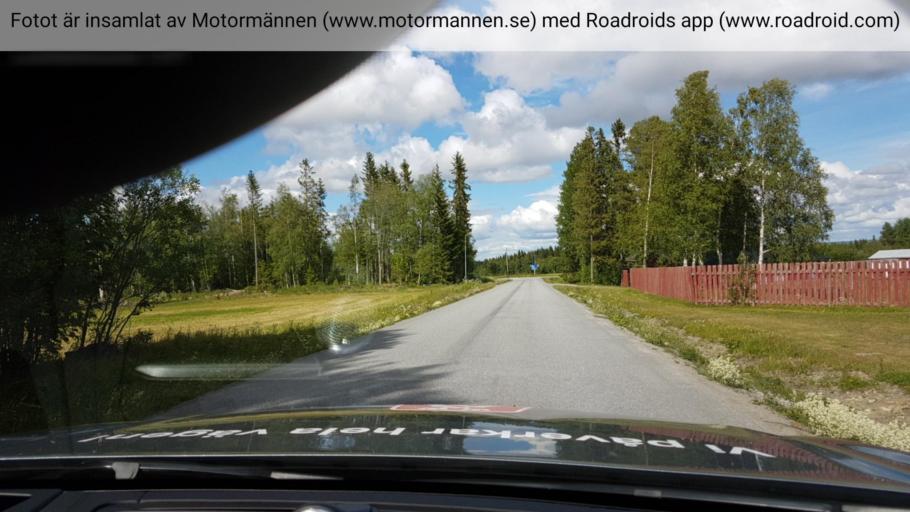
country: SE
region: Jaemtland
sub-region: Bergs Kommun
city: Hoverberg
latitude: 62.9142
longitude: 14.3165
